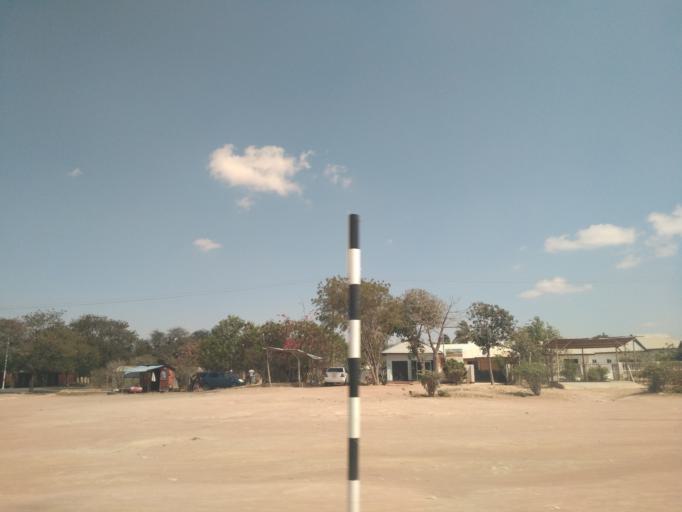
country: TZ
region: Dodoma
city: Dodoma
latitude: -6.1524
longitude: 35.7255
